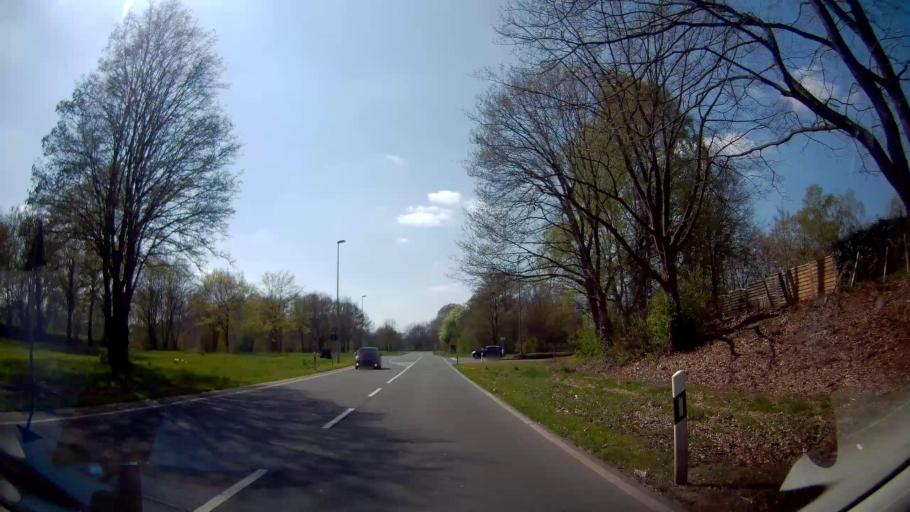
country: DE
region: North Rhine-Westphalia
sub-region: Regierungsbezirk Munster
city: Klein Reken
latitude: 51.7265
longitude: 7.0443
